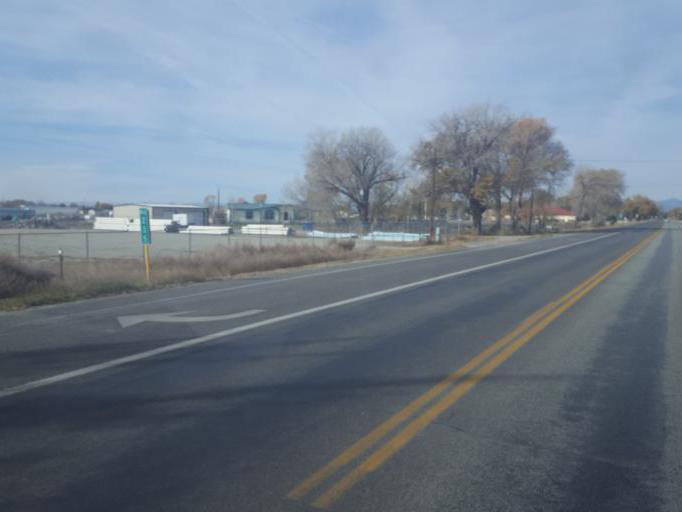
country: US
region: Colorado
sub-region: Alamosa County
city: Alamosa East
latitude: 37.4735
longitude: -105.8369
